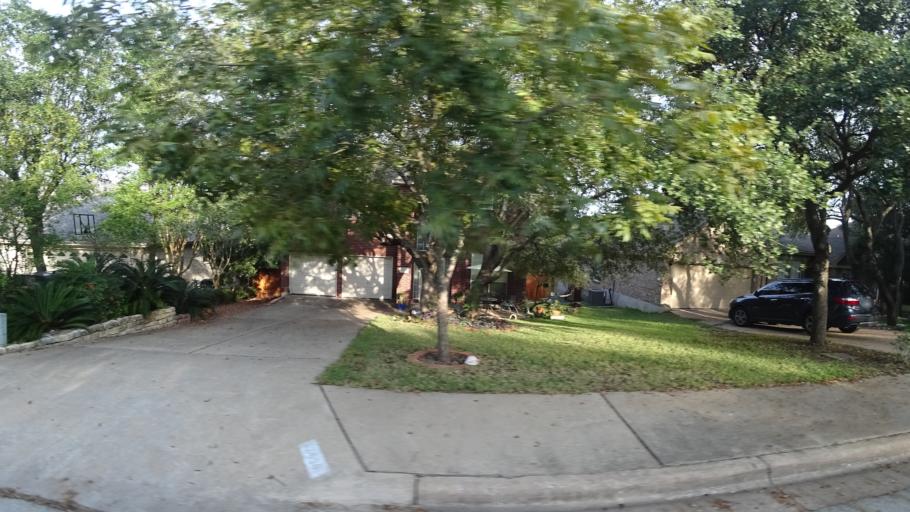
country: US
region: Texas
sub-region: Travis County
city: Hudson Bend
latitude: 30.3777
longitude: -97.8874
